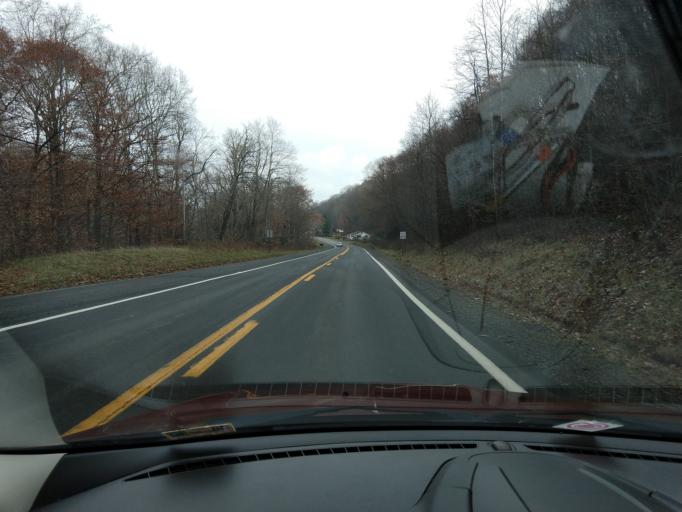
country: US
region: West Virginia
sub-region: Greenbrier County
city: Rainelle
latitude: 38.0407
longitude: -80.7281
